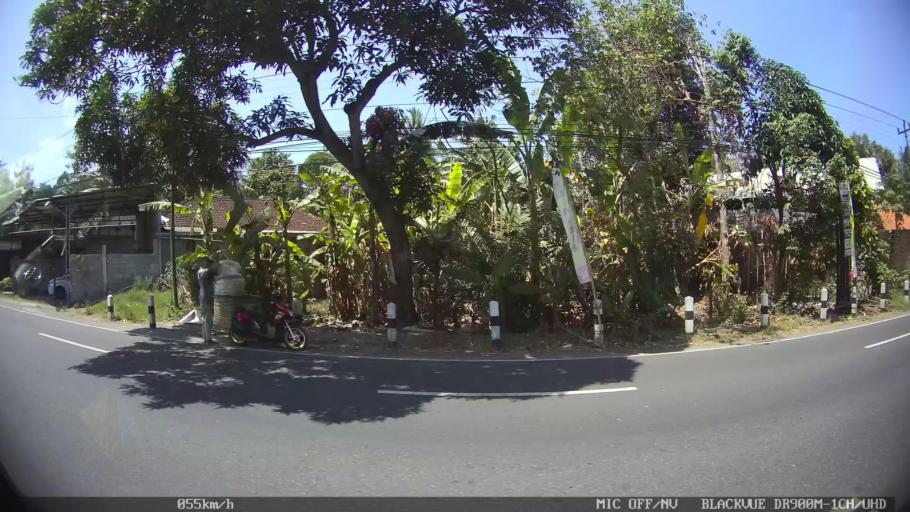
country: ID
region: Daerah Istimewa Yogyakarta
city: Srandakan
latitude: -7.9371
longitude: 110.2581
